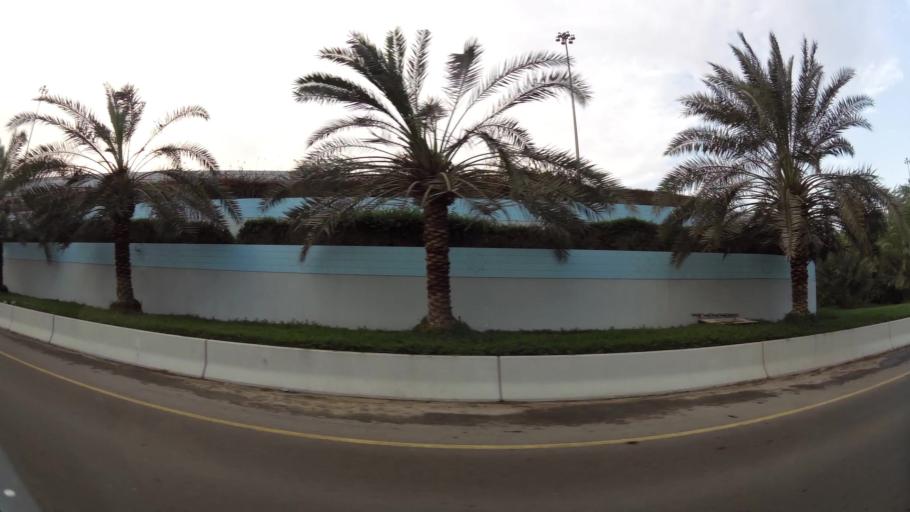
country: AE
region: Abu Dhabi
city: Abu Dhabi
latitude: 24.3909
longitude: 54.5301
